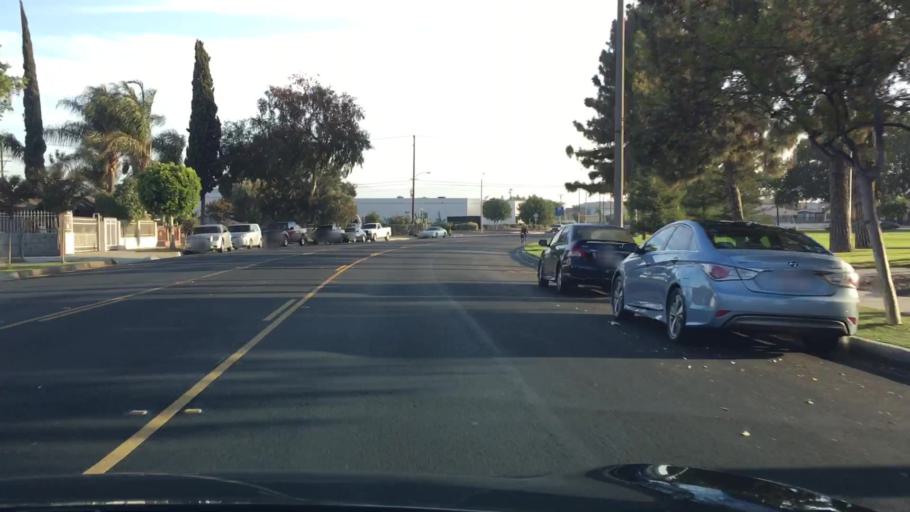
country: US
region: California
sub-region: San Bernardino County
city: Ontario
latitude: 34.0528
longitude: -117.6367
